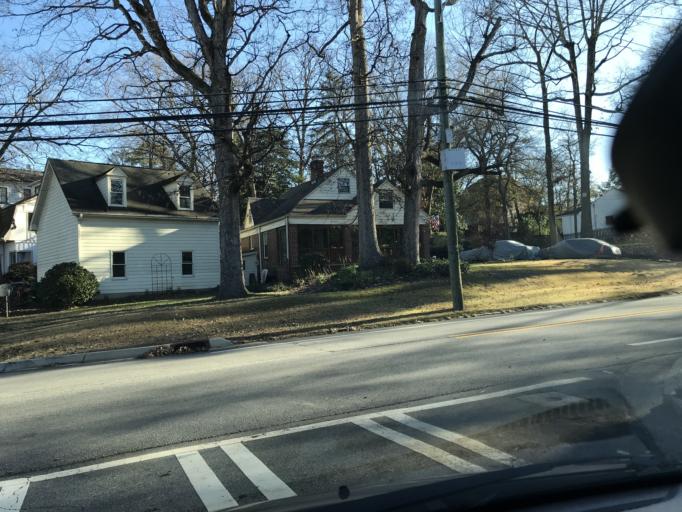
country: US
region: Georgia
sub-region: DeKalb County
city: North Atlanta
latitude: 33.8671
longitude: -84.3394
